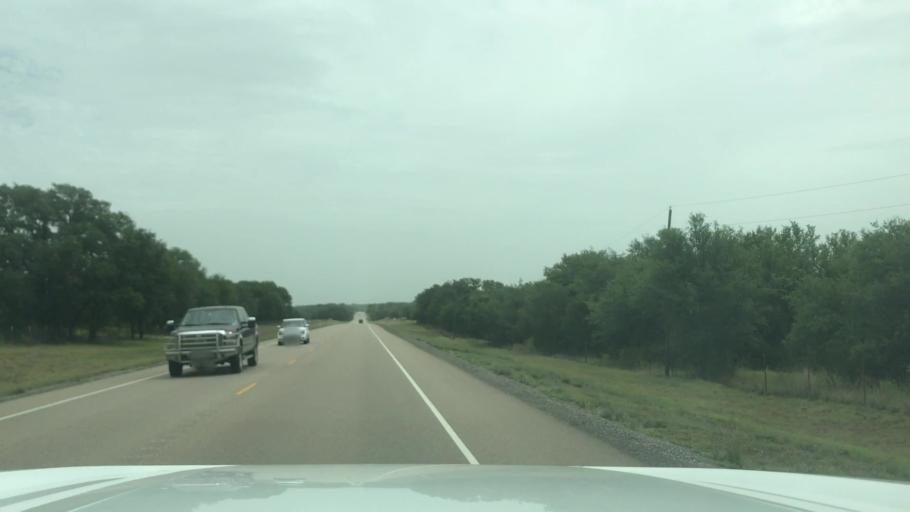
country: US
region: Texas
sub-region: Hamilton County
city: Hico
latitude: 31.9780
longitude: -97.9061
